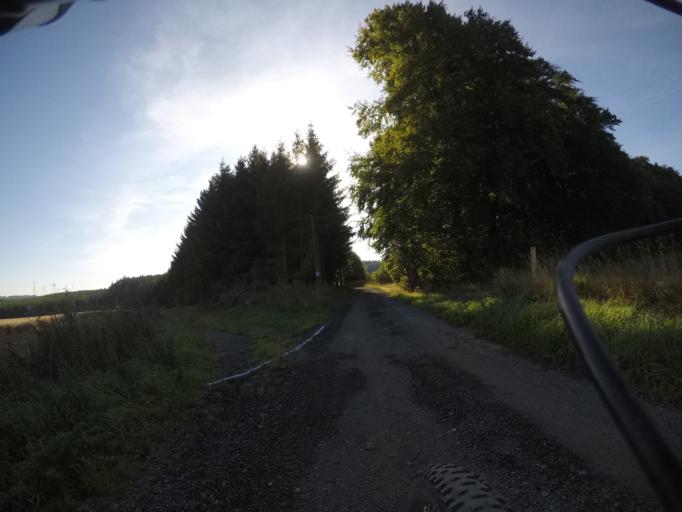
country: BE
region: Wallonia
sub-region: Province du Luxembourg
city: Fauvillers
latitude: 49.9079
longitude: 5.6652
